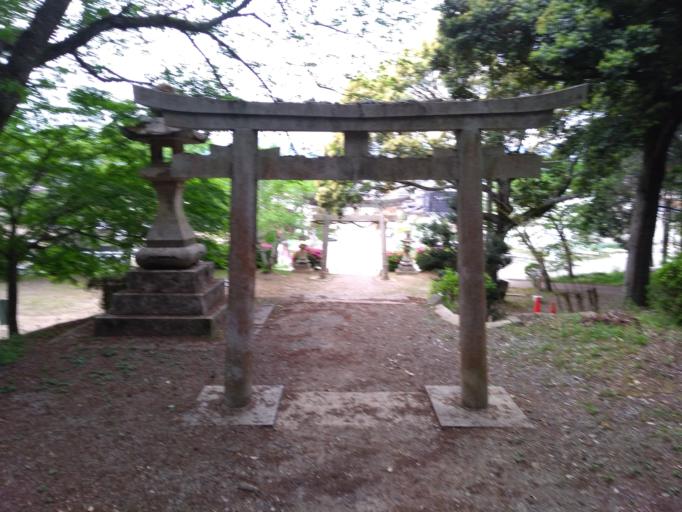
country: JP
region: Yamaguchi
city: Yamaguchi-shi
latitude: 34.1381
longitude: 131.4618
